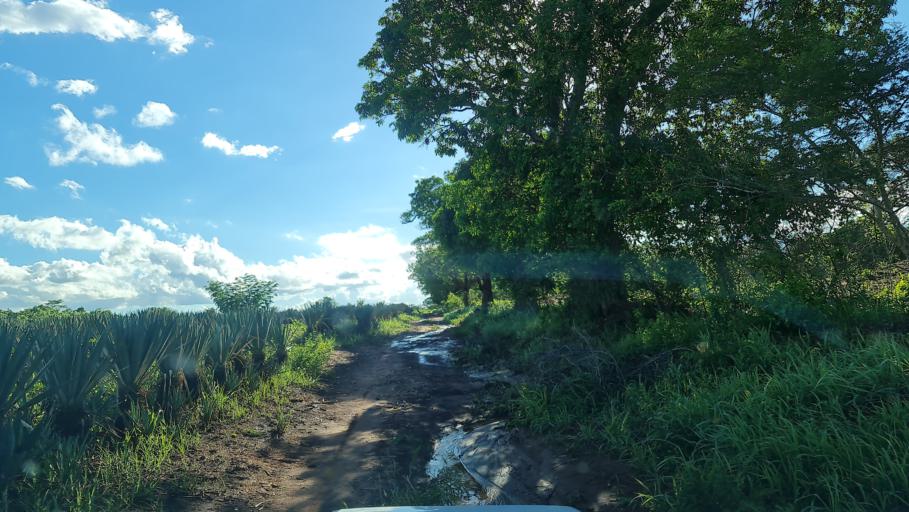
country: MZ
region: Nampula
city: Ilha de Mocambique
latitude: -14.9347
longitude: 40.2099
